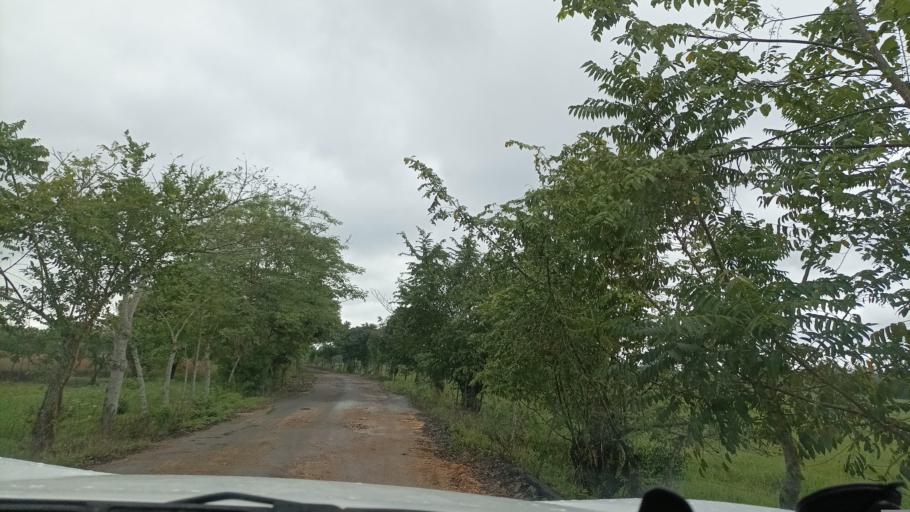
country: MX
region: Veracruz
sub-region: Moloacan
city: Cuichapa
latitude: 17.7738
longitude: -94.3878
